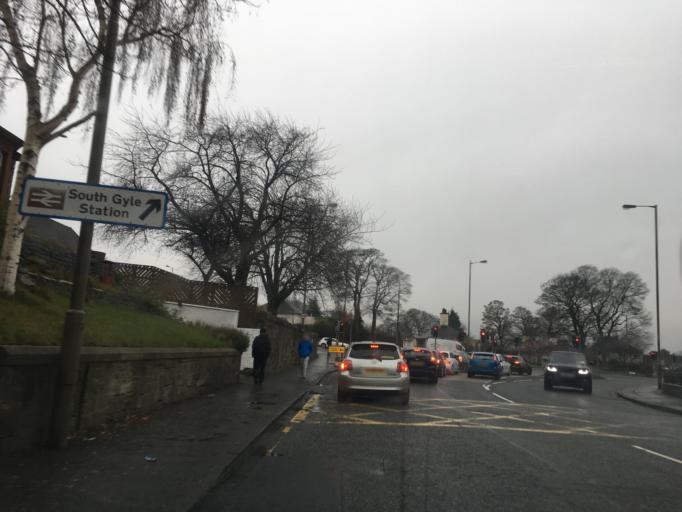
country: GB
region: Scotland
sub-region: Edinburgh
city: Currie
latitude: 55.9408
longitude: -3.2923
